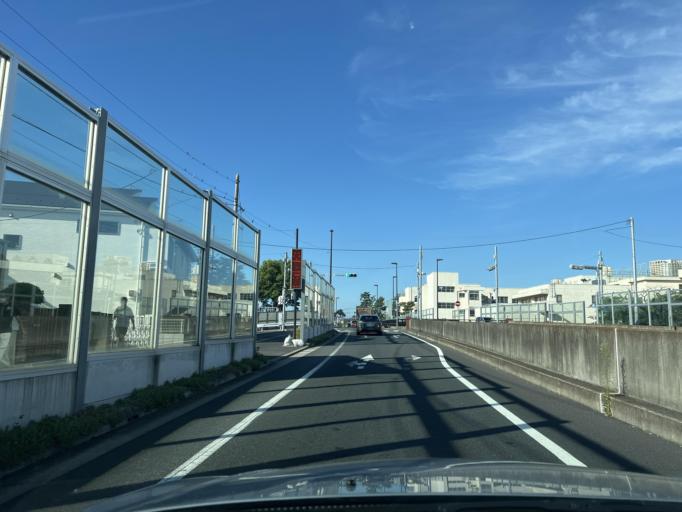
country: JP
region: Chiba
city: Funabashi
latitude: 35.7278
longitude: 139.9389
